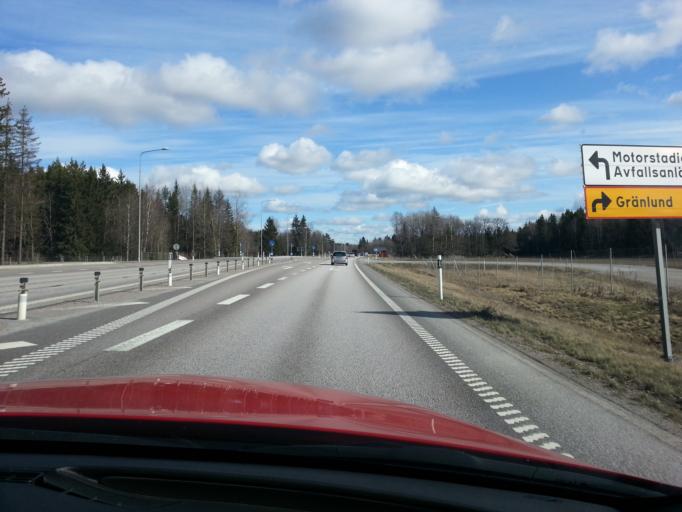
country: SE
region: Uppsala
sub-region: Uppsala Kommun
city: Storvreta
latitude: 59.9245
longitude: 17.7743
